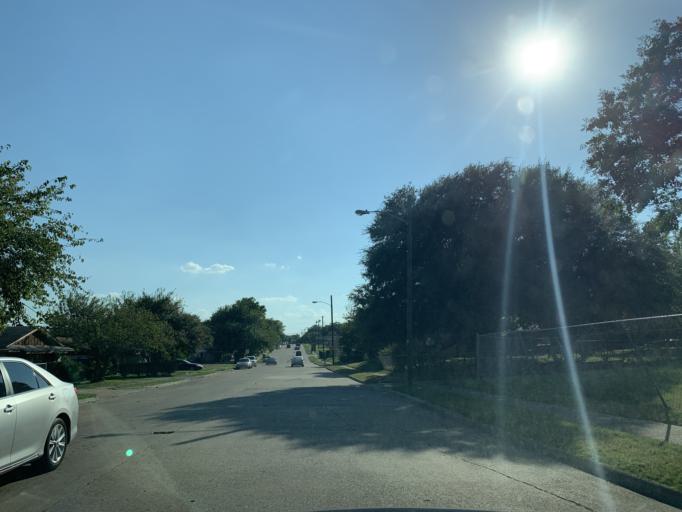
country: US
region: Texas
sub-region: Dallas County
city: Hutchins
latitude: 32.6609
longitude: -96.7626
